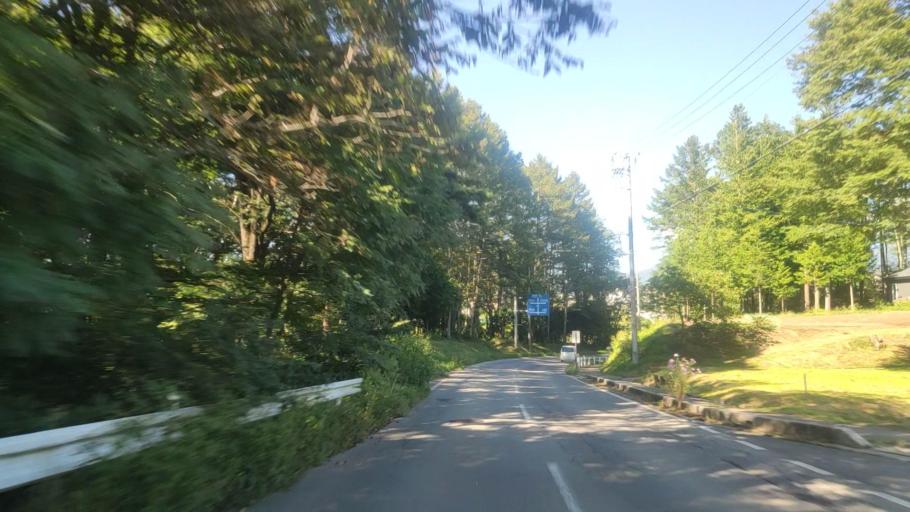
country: JP
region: Nagano
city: Chino
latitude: 36.0088
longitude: 138.2088
